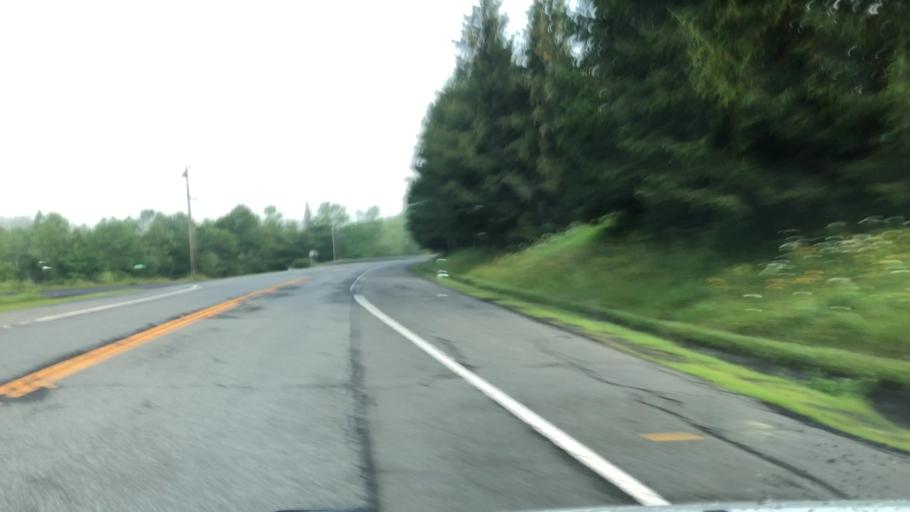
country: US
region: Massachusetts
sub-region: Berkshire County
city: Hinsdale
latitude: 42.5003
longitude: -73.0333
